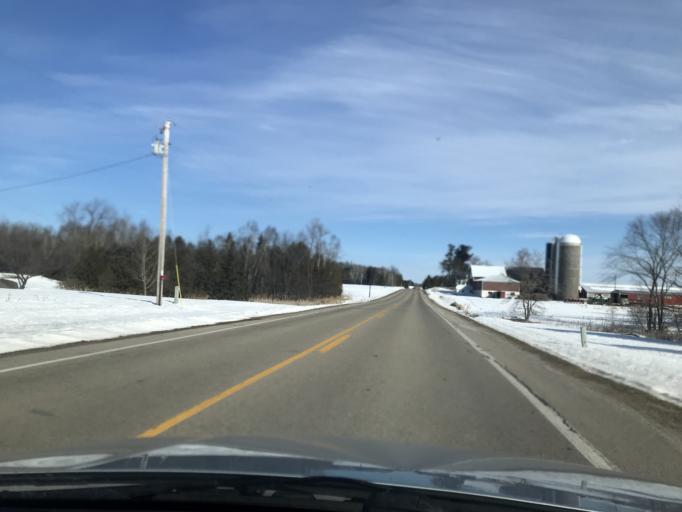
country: US
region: Wisconsin
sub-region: Oconto County
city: Oconto Falls
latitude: 44.9124
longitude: -88.1551
